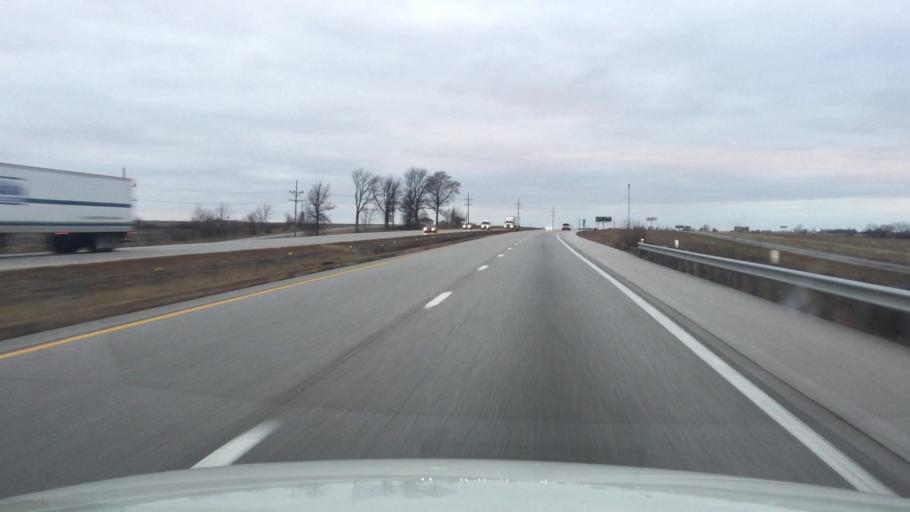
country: US
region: Missouri
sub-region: Saline County
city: Sweet Springs
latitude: 38.9790
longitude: -93.4634
